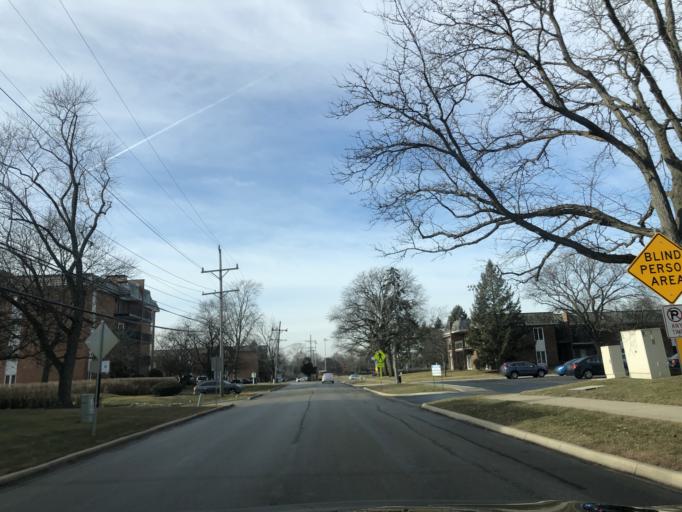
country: US
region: Illinois
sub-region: DuPage County
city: Downers Grove
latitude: 41.8112
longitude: -88.0133
